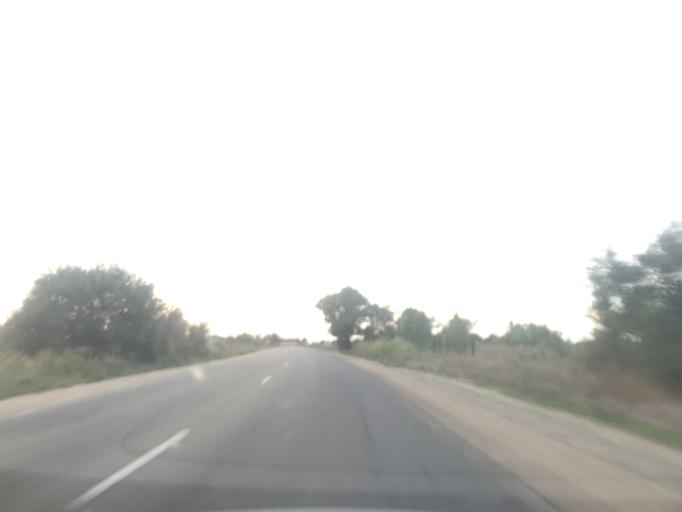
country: FR
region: Provence-Alpes-Cote d'Azur
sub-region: Departement des Bouches-du-Rhone
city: Saintes-Maries-de-la-Mer
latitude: 43.4764
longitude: 4.4088
